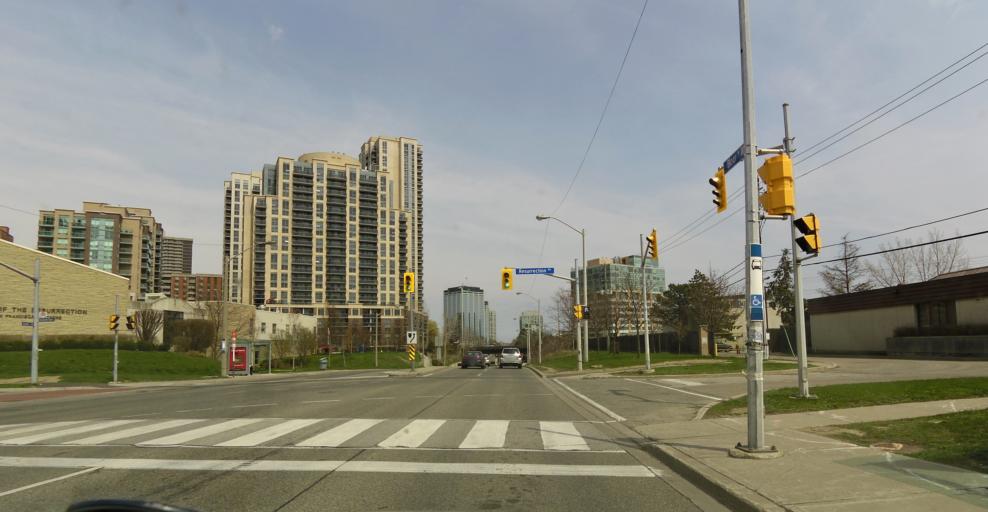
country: CA
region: Ontario
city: Etobicoke
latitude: 43.6430
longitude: -79.5310
